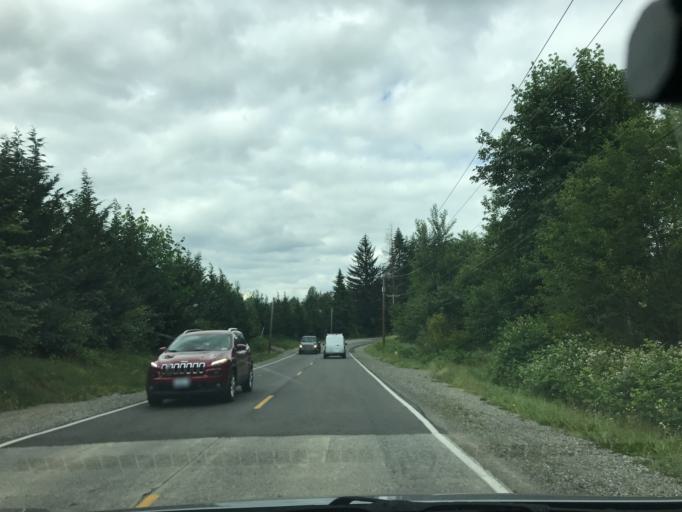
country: US
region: Washington
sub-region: King County
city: Black Diamond
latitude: 47.3141
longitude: -122.0101
